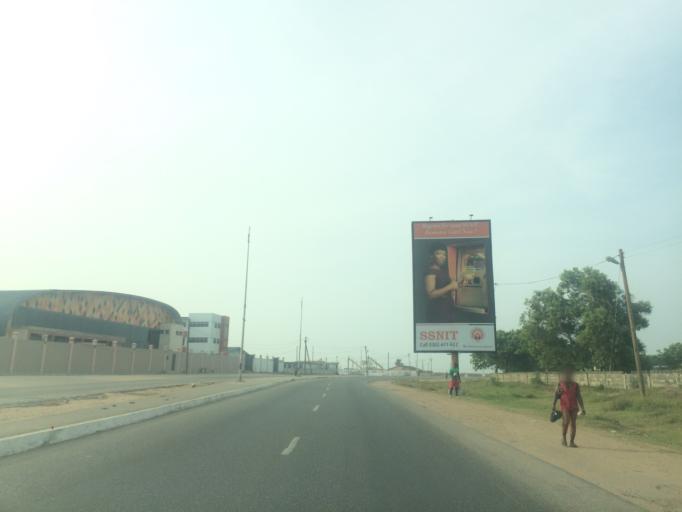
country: GH
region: Greater Accra
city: Accra
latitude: 5.5364
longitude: -0.2216
